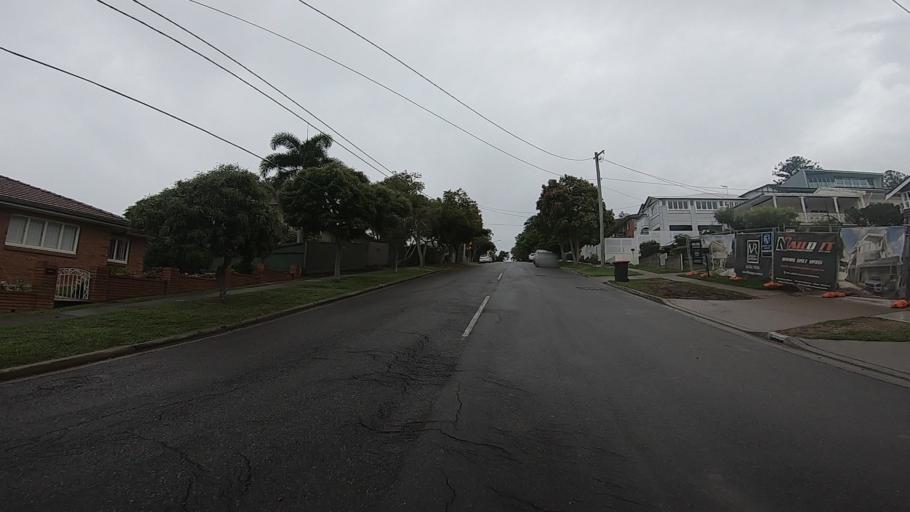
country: AU
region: Queensland
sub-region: Brisbane
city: Ascot
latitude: -27.4319
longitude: 153.0482
